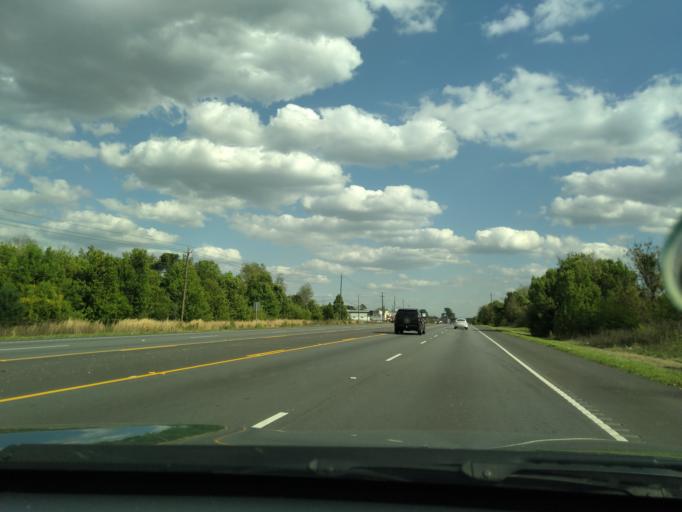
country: US
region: South Carolina
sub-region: Florence County
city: Florence
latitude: 34.2184
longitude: -79.7854
